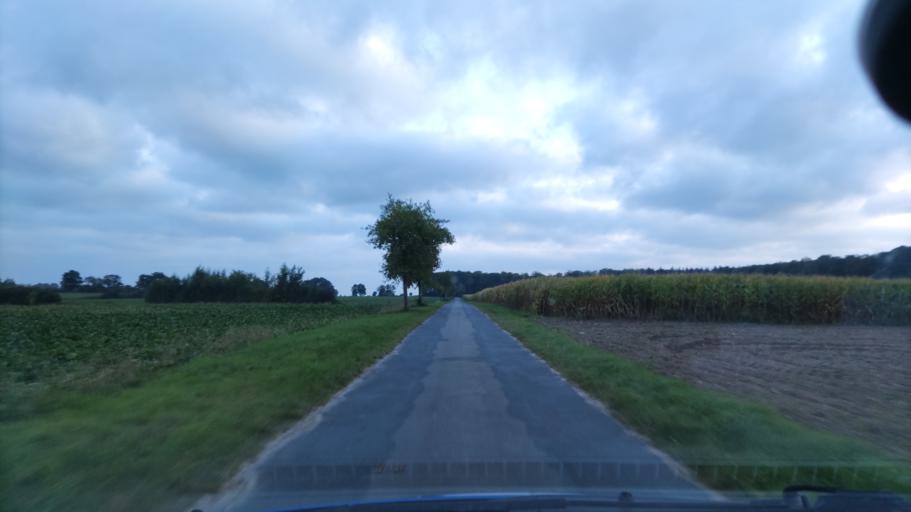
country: DE
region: Lower Saxony
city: Tosterglope
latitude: 53.2293
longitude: 10.8292
